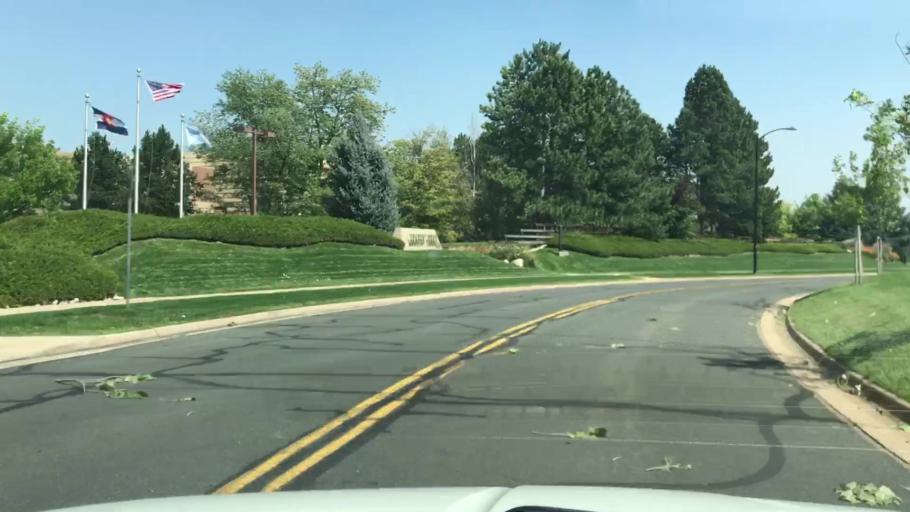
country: US
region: Colorado
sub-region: Boulder County
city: Gunbarrel
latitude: 40.0644
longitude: -105.2141
